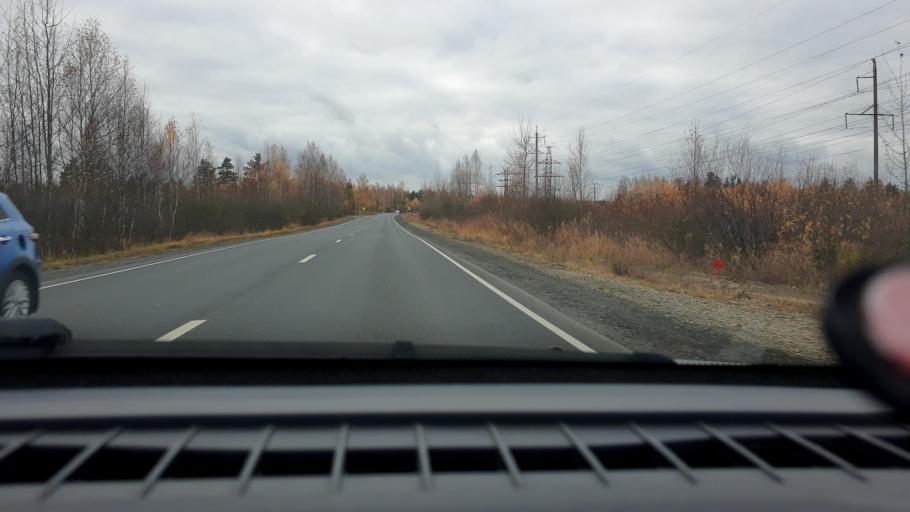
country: RU
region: Nizjnij Novgorod
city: Lukino
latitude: 56.3699
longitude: 43.6187
